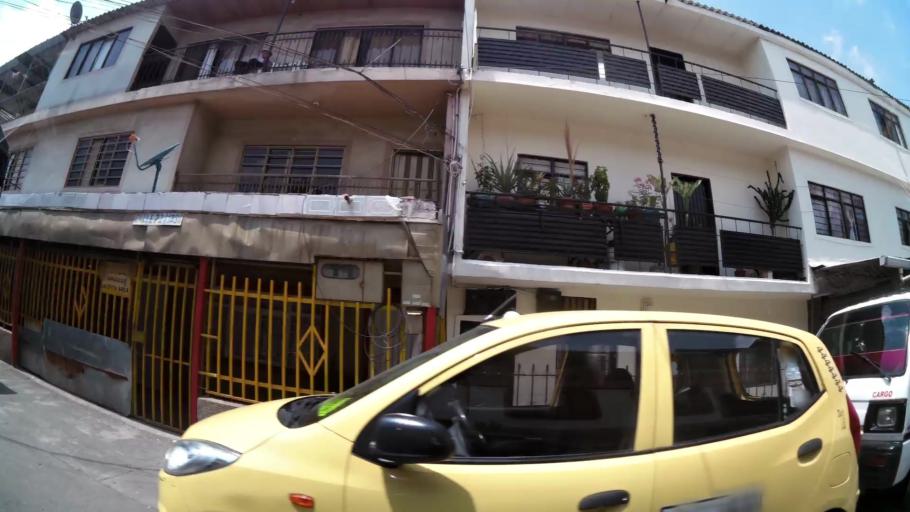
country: CO
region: Valle del Cauca
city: Cali
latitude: 3.4801
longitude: -76.4862
